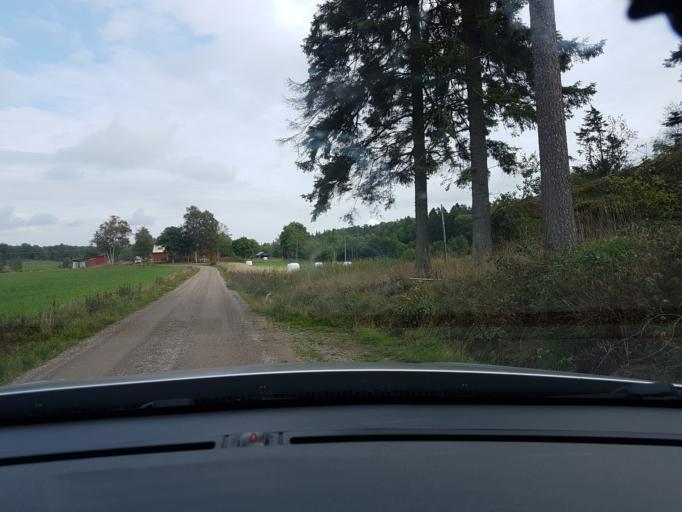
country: SE
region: Vaestra Goetaland
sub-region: Ale Kommun
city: Skepplanda
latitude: 57.8918
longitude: 12.2013
